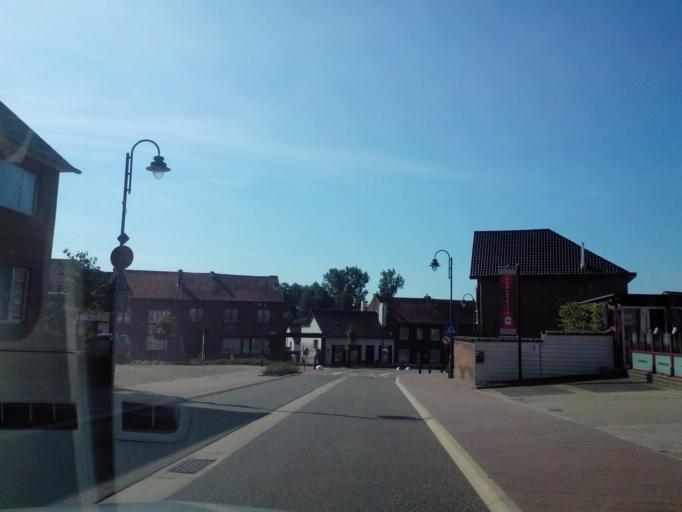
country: BE
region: Flanders
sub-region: Provincie Limburg
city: Opglabbeek
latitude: 51.0446
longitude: 5.5855
